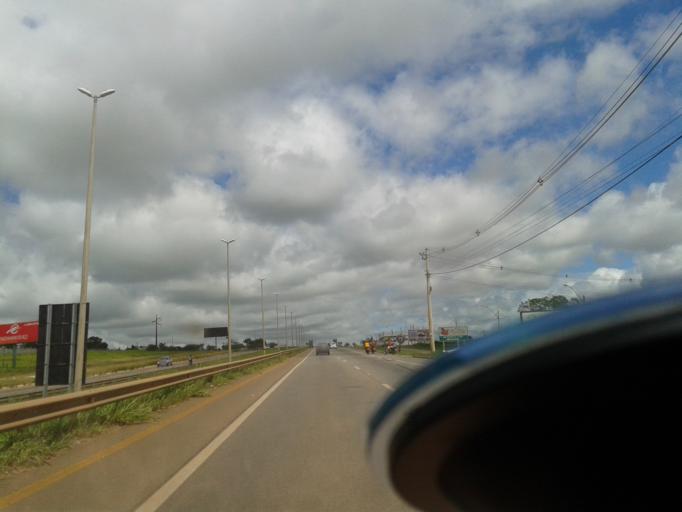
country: BR
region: Goias
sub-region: Goianira
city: Goianira
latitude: -16.5616
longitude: -49.4022
